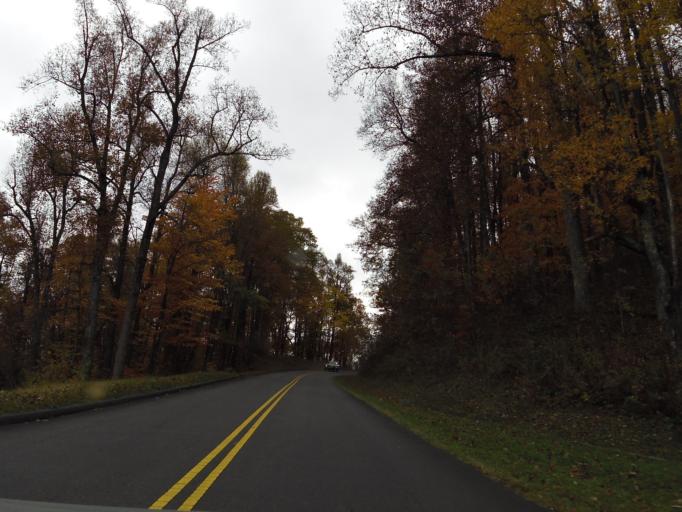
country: US
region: North Carolina
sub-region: Ashe County
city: West Jefferson
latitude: 36.2609
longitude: -81.4418
